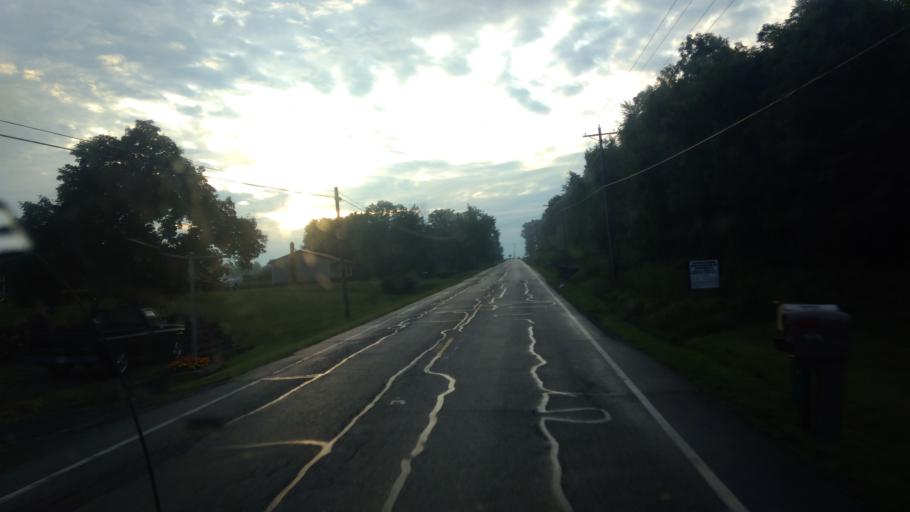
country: US
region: Ohio
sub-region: Guernsey County
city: Byesville
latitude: 39.9855
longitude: -81.3825
